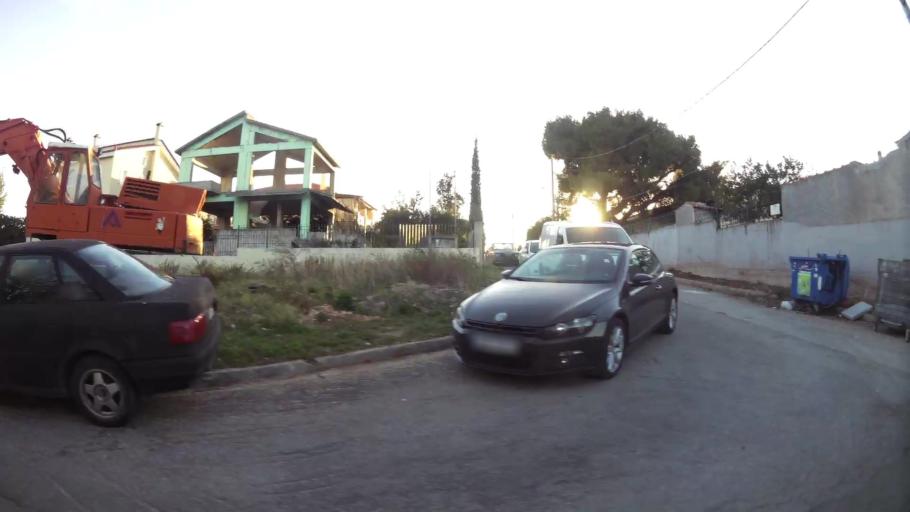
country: GR
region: Attica
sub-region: Nomarchia Anatolikis Attikis
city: Kryoneri
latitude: 38.1458
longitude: 23.8315
